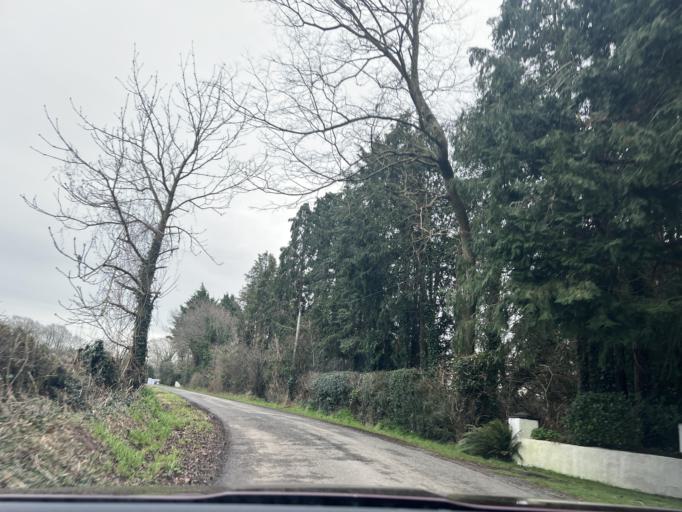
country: IE
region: Leinster
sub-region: Loch Garman
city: Castlebridge
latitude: 52.3866
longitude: -6.5296
